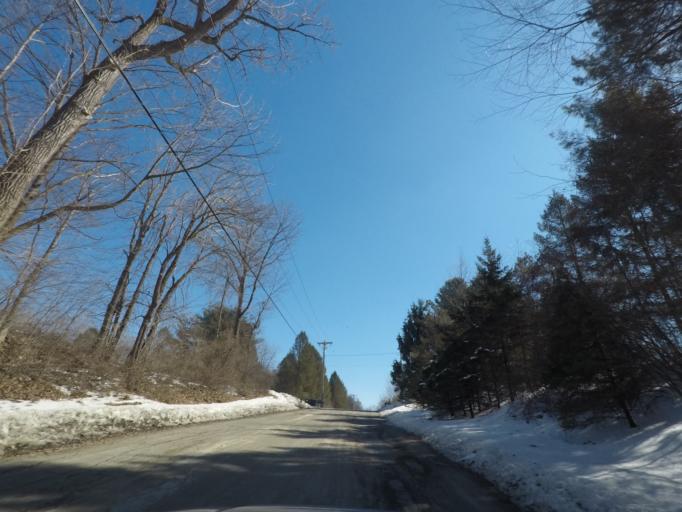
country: US
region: New York
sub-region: Saratoga County
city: Stillwater
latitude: 42.9243
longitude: -73.6272
